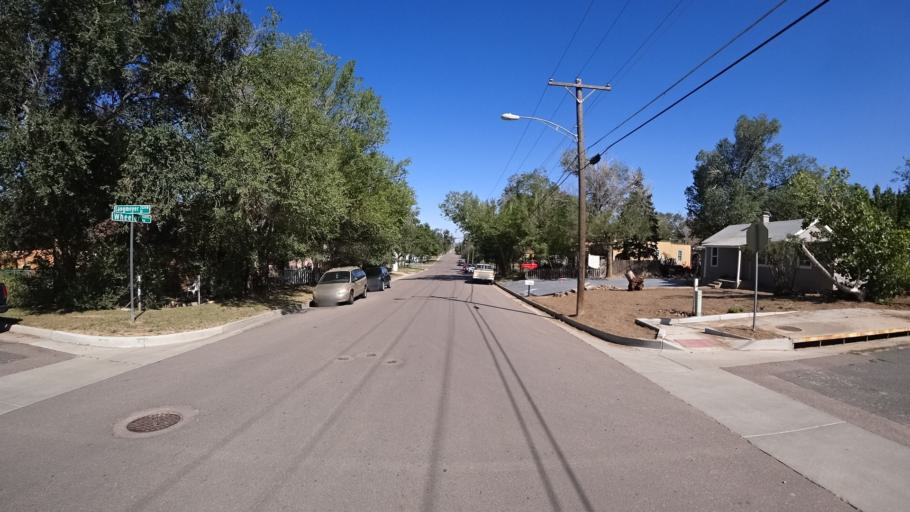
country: US
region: Colorado
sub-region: El Paso County
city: Colorado Springs
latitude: 38.8354
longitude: -104.8704
